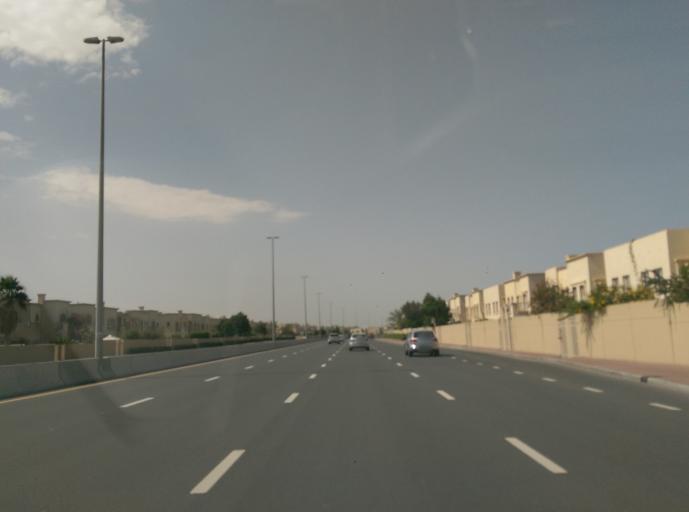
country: AE
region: Dubai
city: Dubai
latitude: 25.0649
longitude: 55.1895
